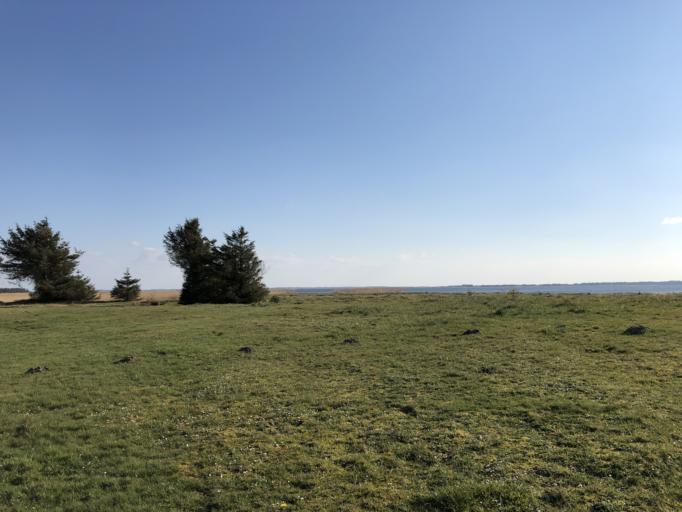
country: DK
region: Central Jutland
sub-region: Holstebro Kommune
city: Ulfborg
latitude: 56.3501
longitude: 8.2471
